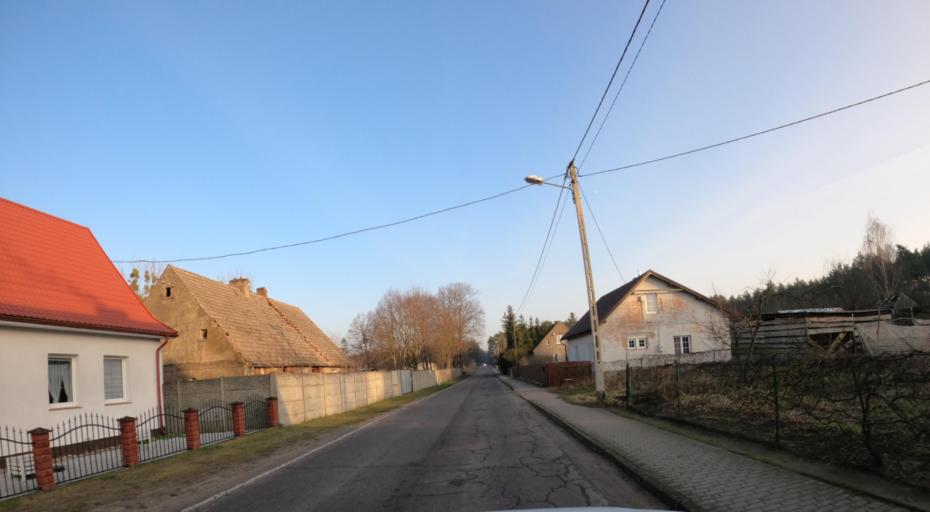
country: PL
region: West Pomeranian Voivodeship
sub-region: Powiat mysliborski
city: Debno
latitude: 52.7124
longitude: 14.6586
